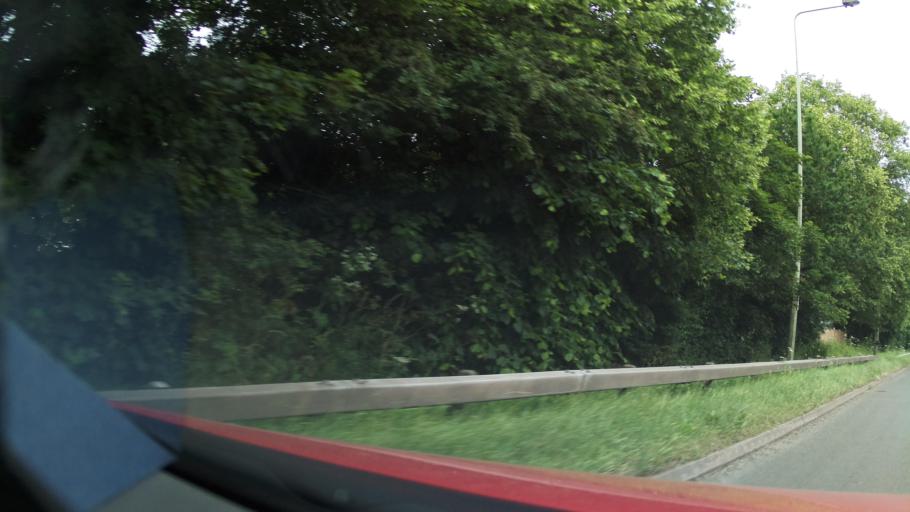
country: GB
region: England
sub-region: Staffordshire
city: Penkridge
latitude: 52.7003
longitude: -2.1280
